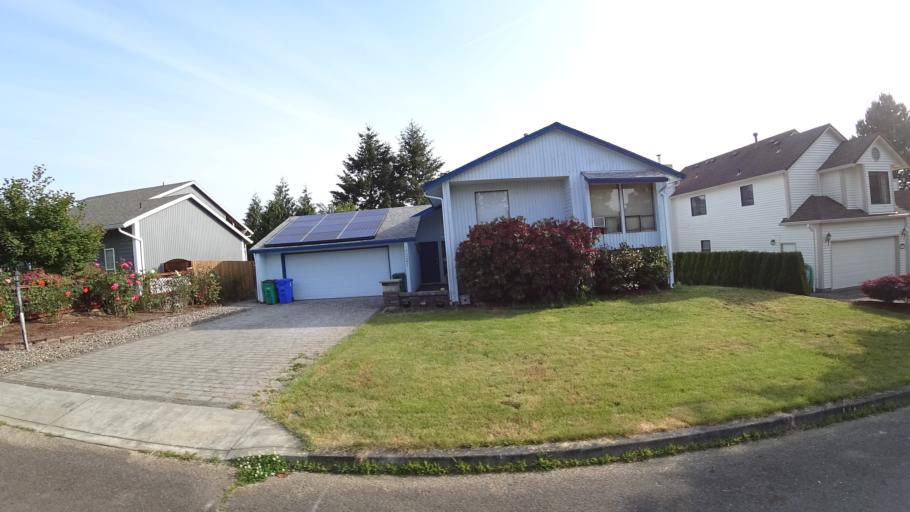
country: US
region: Oregon
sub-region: Clackamas County
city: Happy Valley
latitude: 45.4639
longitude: -122.5158
